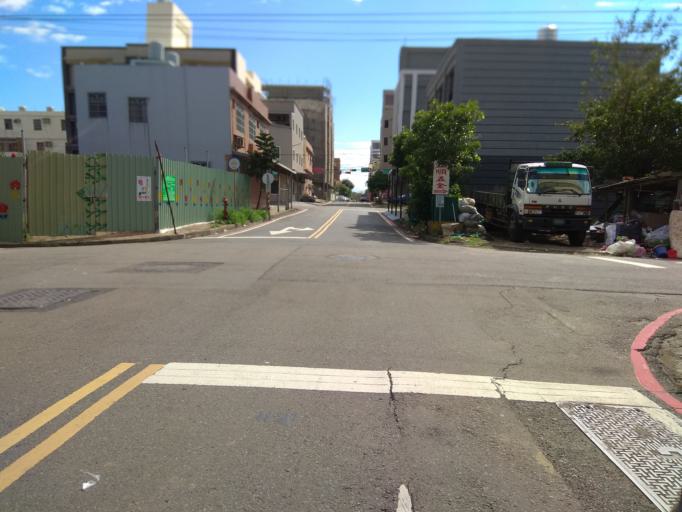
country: TW
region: Taiwan
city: Taoyuan City
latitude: 25.0506
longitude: 121.1191
